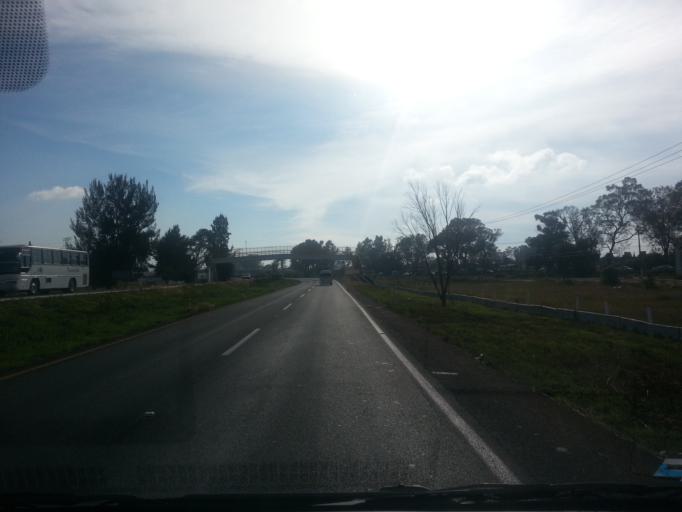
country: MX
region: Mexico
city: Santo Tomas Chiconautla
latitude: 19.6127
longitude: -99.0210
